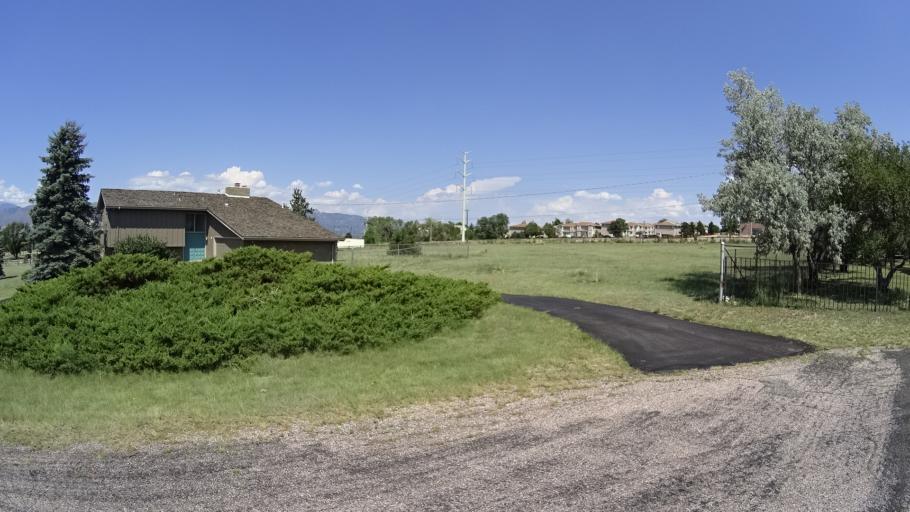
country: US
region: Colorado
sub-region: El Paso County
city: Air Force Academy
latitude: 38.9394
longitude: -104.7781
